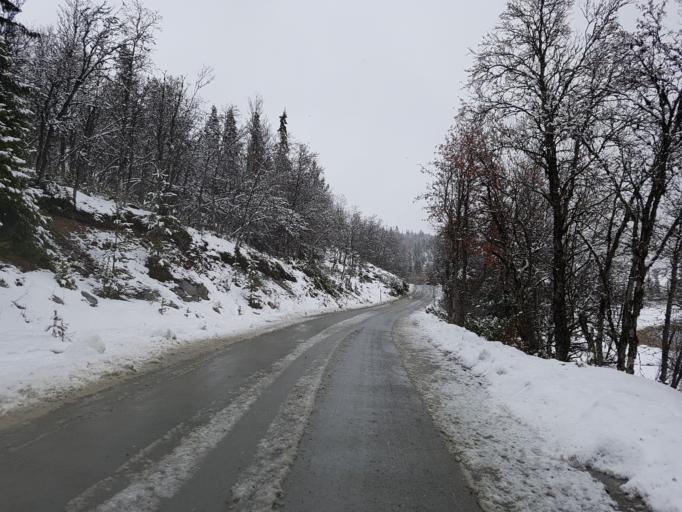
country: NO
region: Oppland
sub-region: Sel
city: Otta
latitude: 61.8023
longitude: 9.7030
